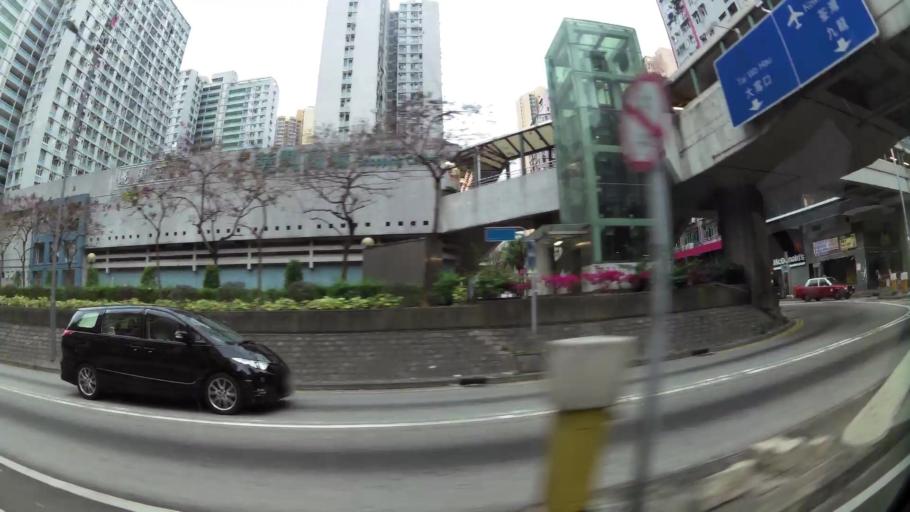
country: HK
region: Tsuen Wan
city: Tsuen Wan
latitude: 22.3667
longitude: 114.1335
